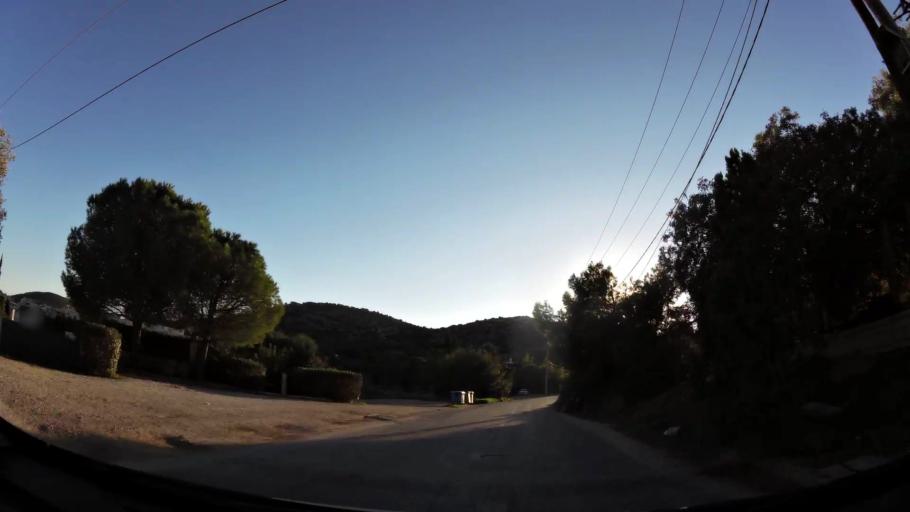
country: GR
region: Attica
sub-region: Nomarchia Anatolikis Attikis
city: Vari
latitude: 37.8240
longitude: 23.7929
